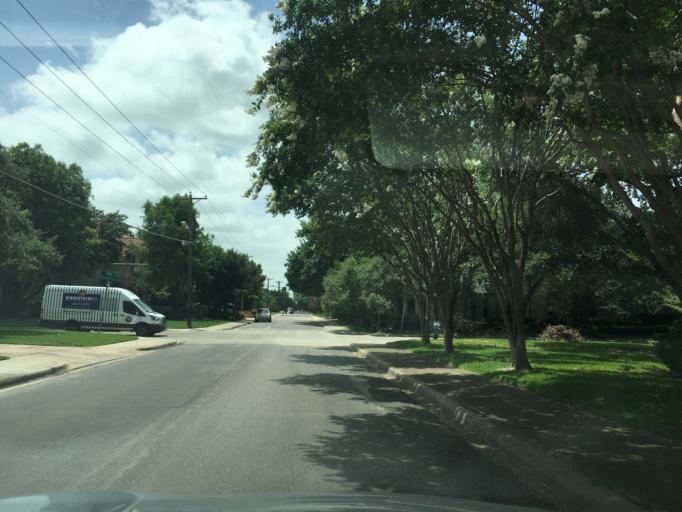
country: US
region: Texas
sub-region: Dallas County
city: University Park
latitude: 32.8919
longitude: -96.7931
